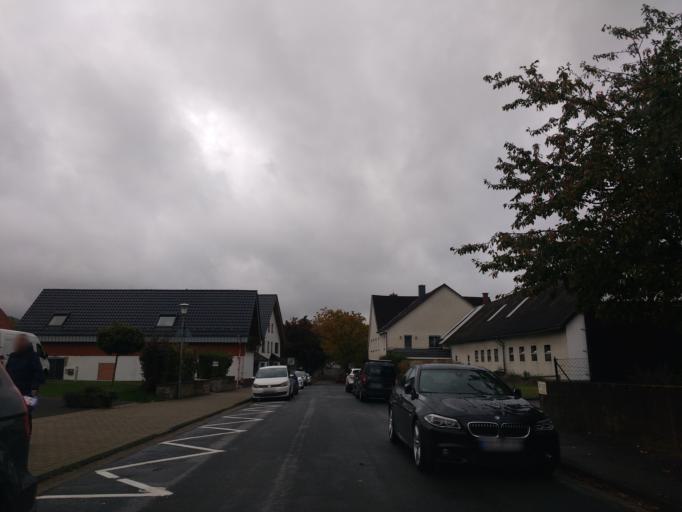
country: DE
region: Lower Saxony
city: Bad Pyrmont
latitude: 51.9885
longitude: 9.2352
